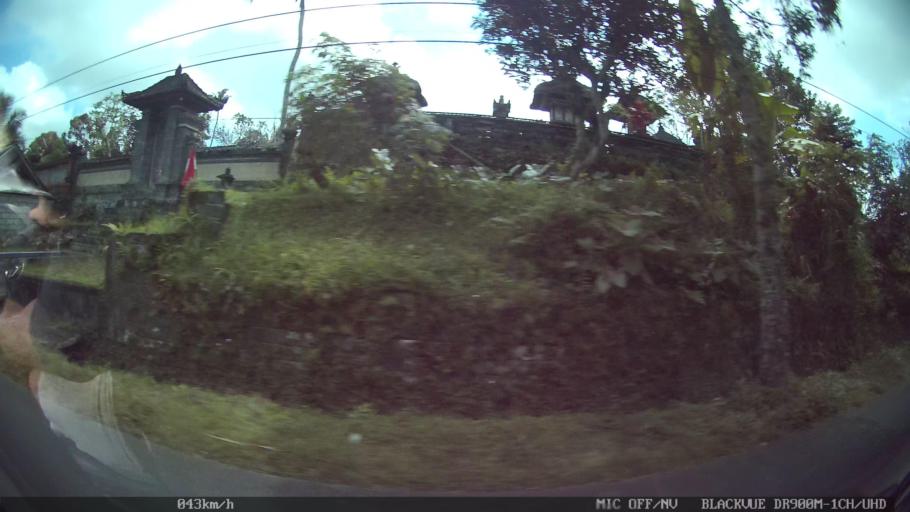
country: ID
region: Bali
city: Banjar Madangan Kaja
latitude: -8.4734
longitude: 115.3243
